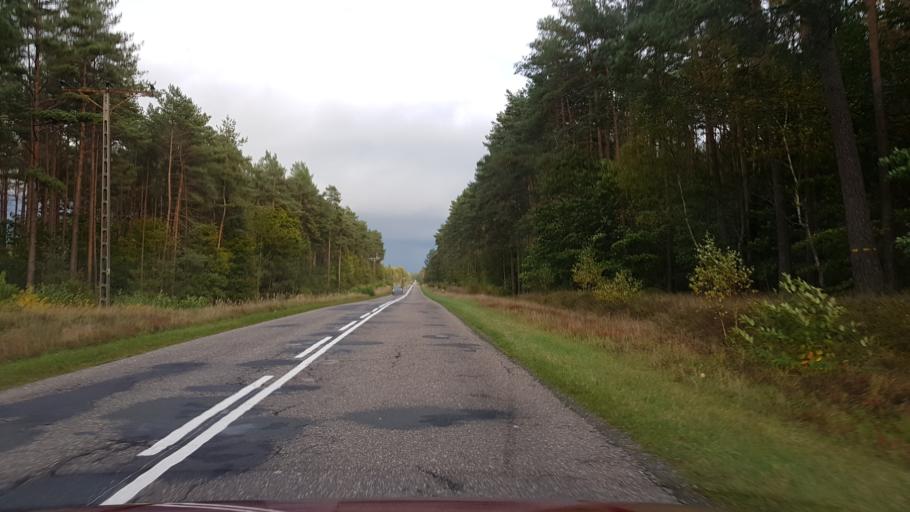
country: PL
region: West Pomeranian Voivodeship
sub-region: Powiat walecki
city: Tuczno
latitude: 53.1686
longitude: 16.2929
